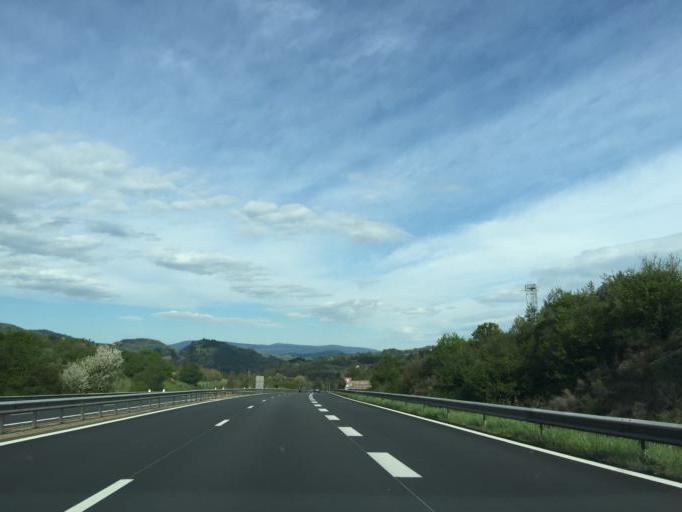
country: FR
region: Rhone-Alpes
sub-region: Departement de la Loire
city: Saint-Just-en-Chevalet
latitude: 45.8712
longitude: 3.9262
